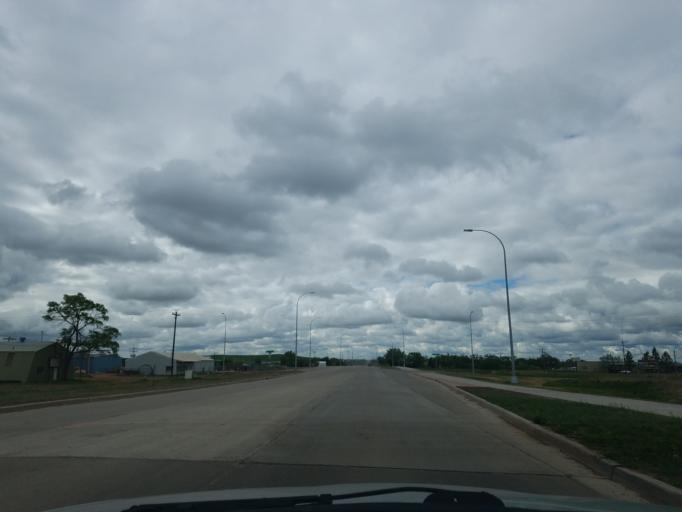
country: US
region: North Dakota
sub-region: McKenzie County
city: Watford City
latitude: 47.7911
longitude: -103.2832
